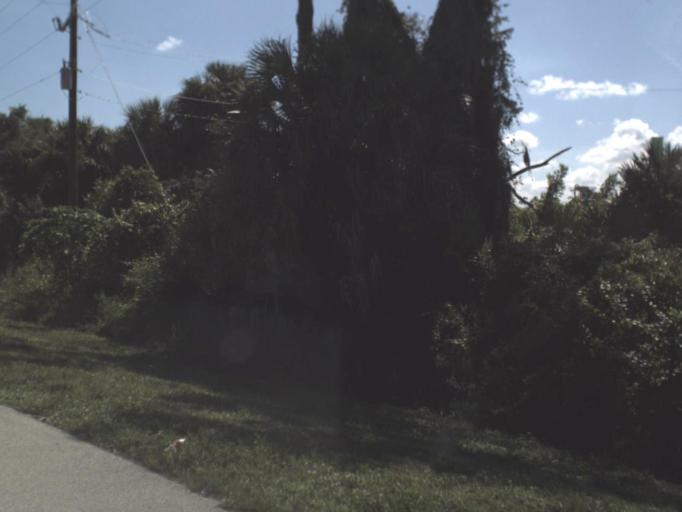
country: US
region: Florida
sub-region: Hendry County
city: Port LaBelle
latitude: 26.8159
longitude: -81.2999
